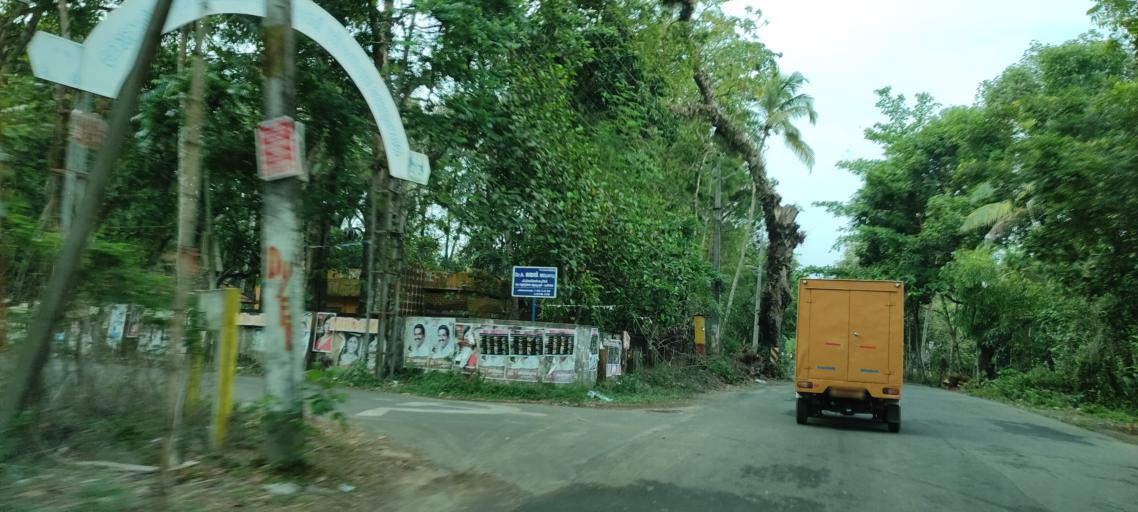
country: IN
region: Kerala
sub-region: Kottayam
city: Vaikam
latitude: 9.7666
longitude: 76.3626
